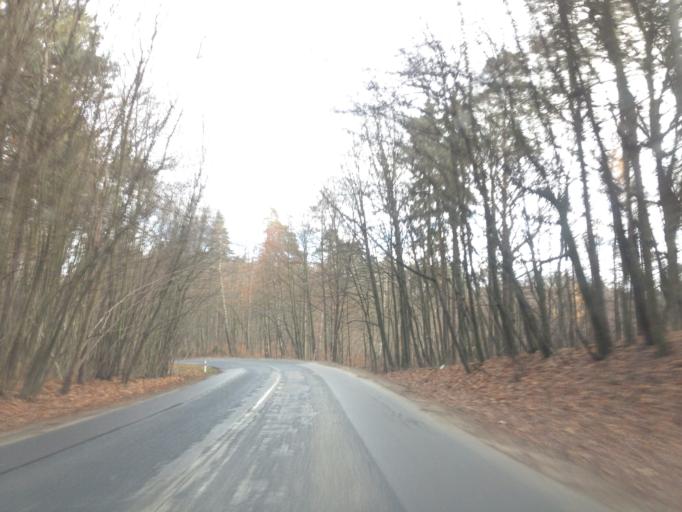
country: PL
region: Pomeranian Voivodeship
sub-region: Powiat gdanski
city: Kolbudy
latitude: 54.2674
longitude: 18.4315
